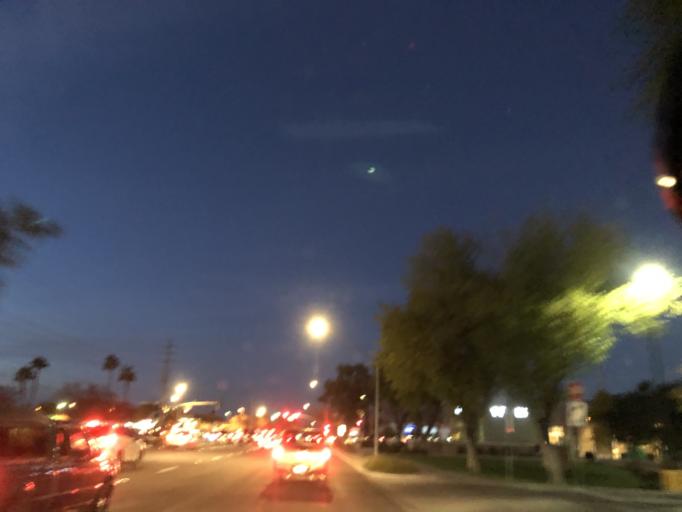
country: US
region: Arizona
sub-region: Maricopa County
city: Peoria
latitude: 33.6375
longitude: -112.1862
